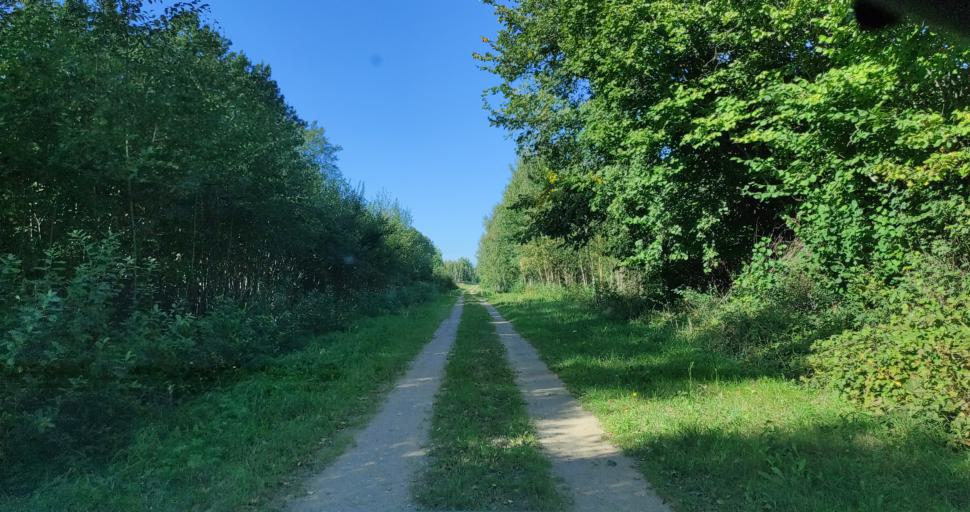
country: LV
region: Kuldigas Rajons
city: Kuldiga
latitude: 56.9745
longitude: 21.9214
